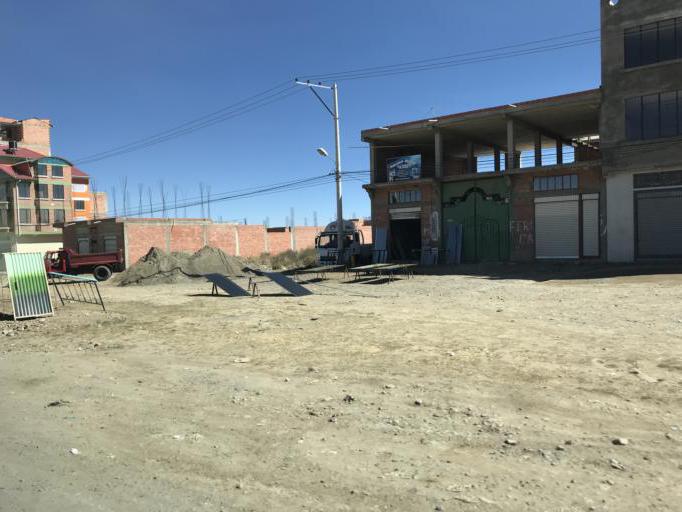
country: BO
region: La Paz
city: La Paz
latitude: -16.5071
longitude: -68.2592
